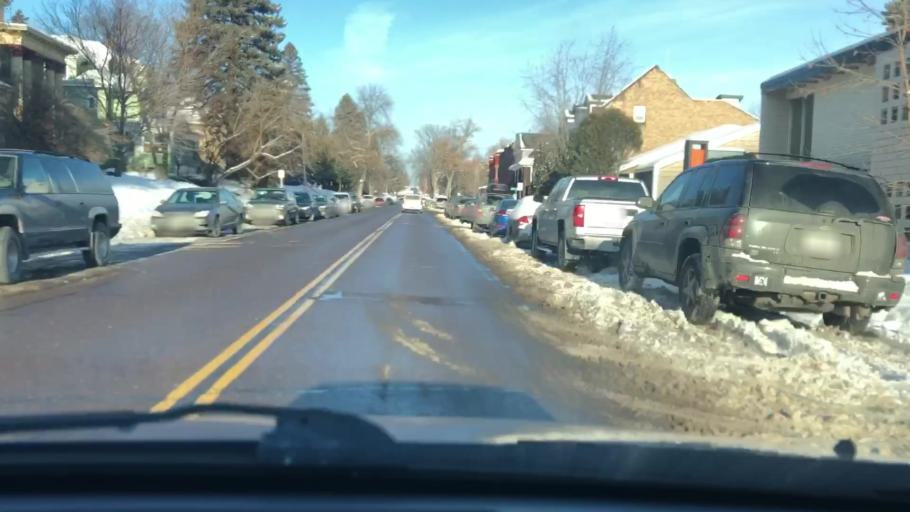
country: US
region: Minnesota
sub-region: Saint Louis County
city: Duluth
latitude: 46.8016
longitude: -92.0790
